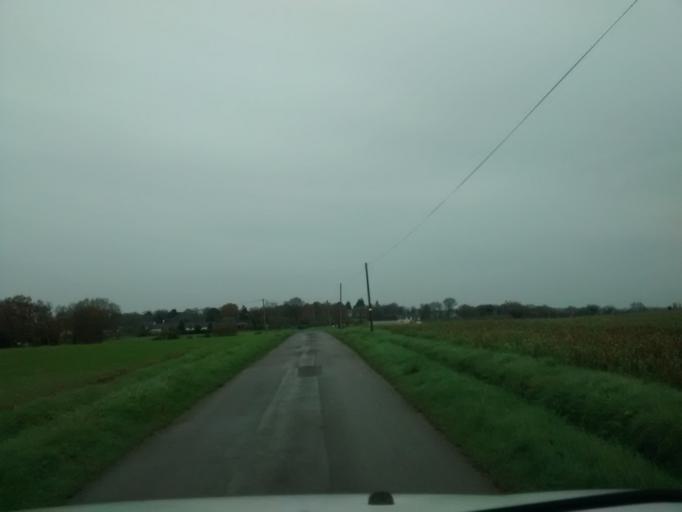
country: FR
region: Brittany
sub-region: Departement d'Ille-et-Vilaine
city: Acigne
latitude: 48.1296
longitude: -1.5539
